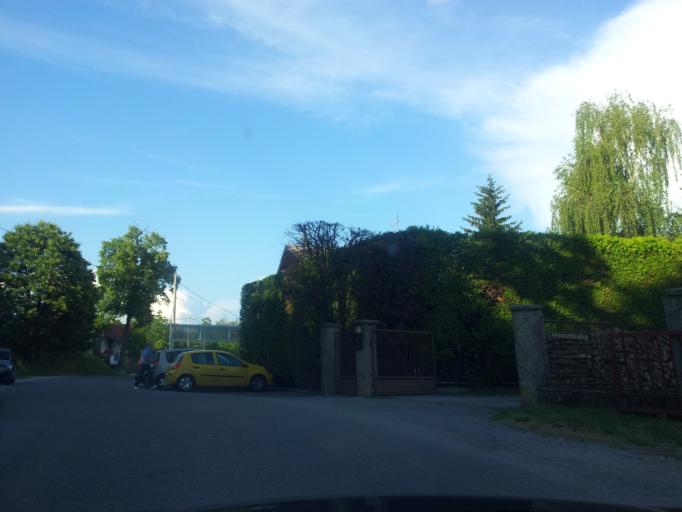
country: HR
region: Karlovacka
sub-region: Grad Karlovac
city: Karlovac
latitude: 45.4944
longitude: 15.5082
